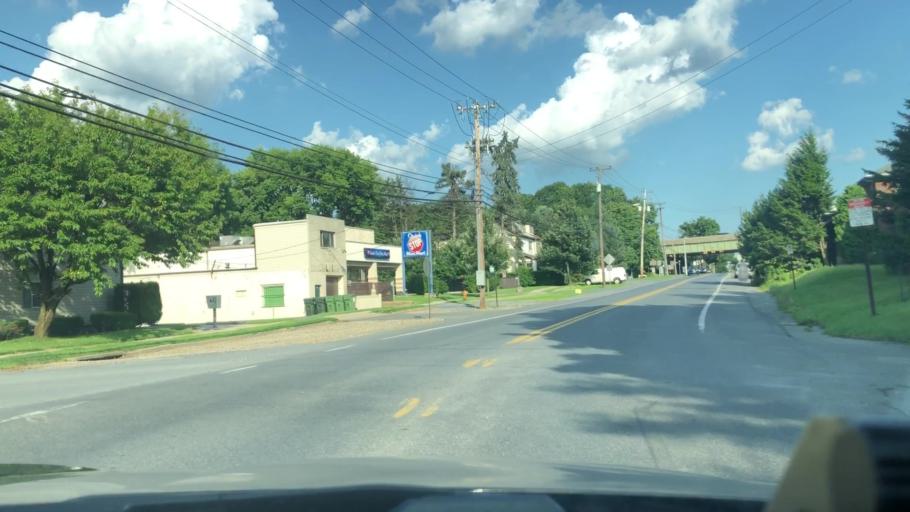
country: US
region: Pennsylvania
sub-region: Lehigh County
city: Allentown
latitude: 40.6170
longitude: -75.5083
